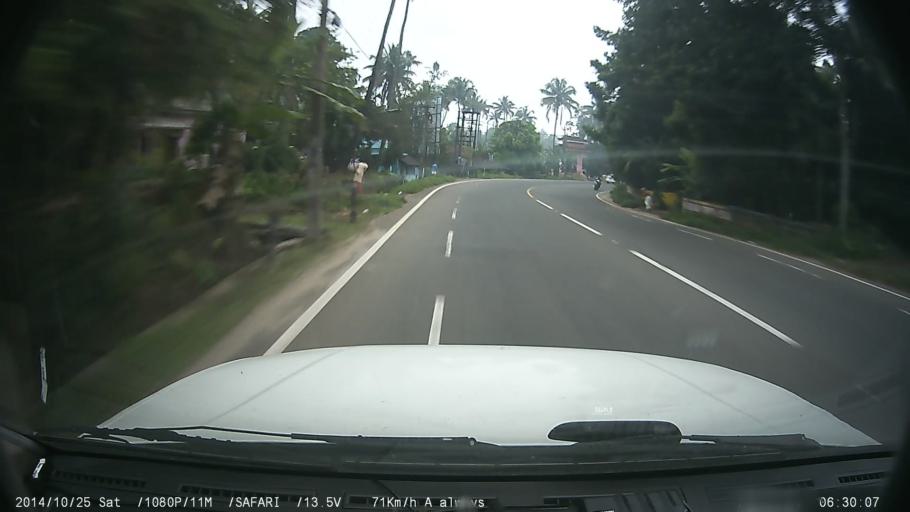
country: IN
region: Kerala
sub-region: Ernakulam
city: Muvattupula
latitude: 10.0359
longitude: 76.5451
